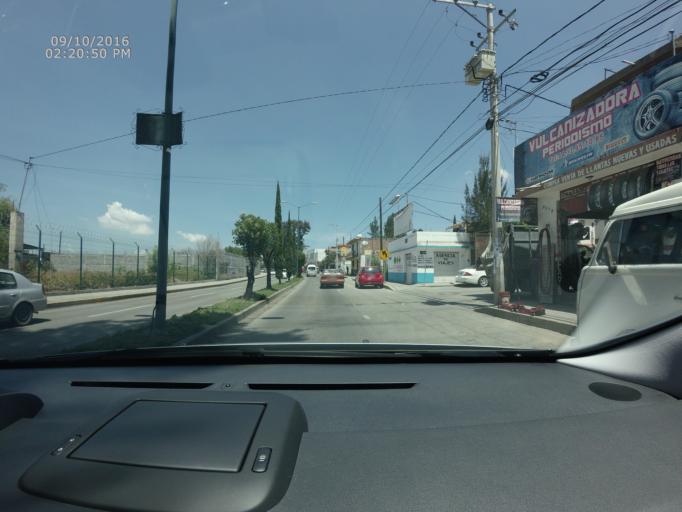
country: MX
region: Michoacan
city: Morelia
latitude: 19.6956
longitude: -101.2193
